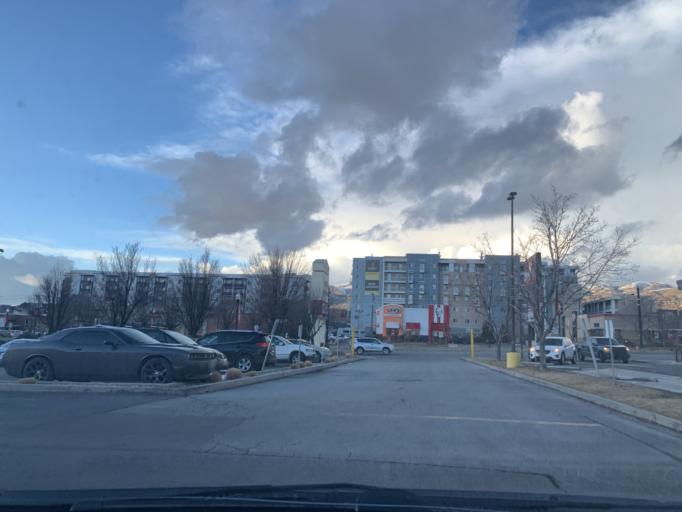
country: US
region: Utah
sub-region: Salt Lake County
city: Salt Lake City
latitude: 40.7600
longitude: -111.8750
